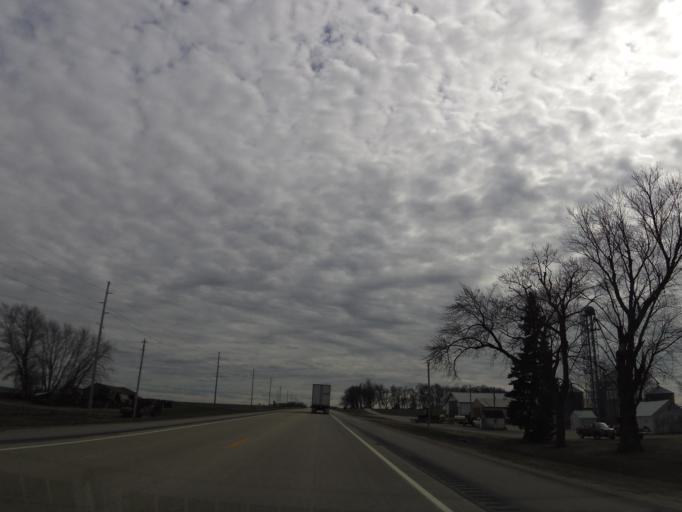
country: US
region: Minnesota
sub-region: Fillmore County
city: Spring Valley
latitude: 43.5910
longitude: -92.3893
